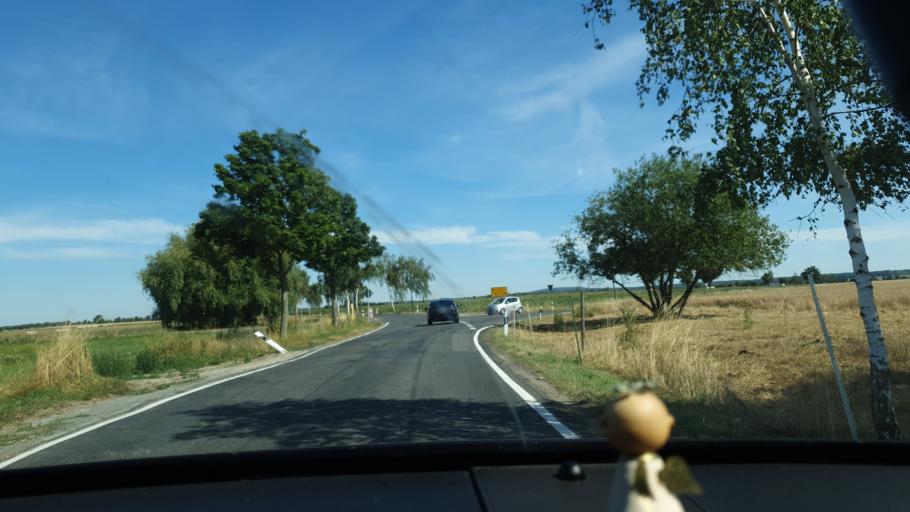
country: DE
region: Saxony
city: Mockrehna
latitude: 51.4808
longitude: 12.7881
